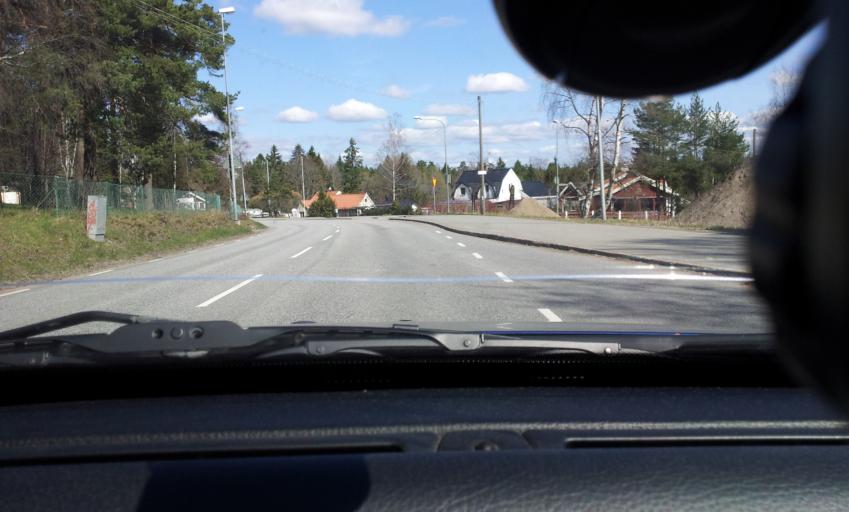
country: SE
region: Stockholm
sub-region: Haninge Kommun
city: Haninge
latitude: 59.1857
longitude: 18.1836
